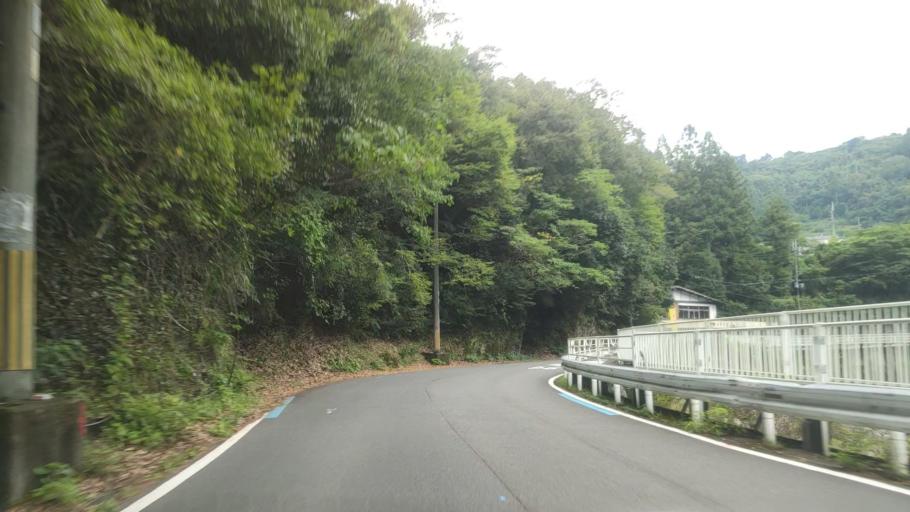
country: JP
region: Wakayama
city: Hashimoto
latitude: 34.2768
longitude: 135.5679
